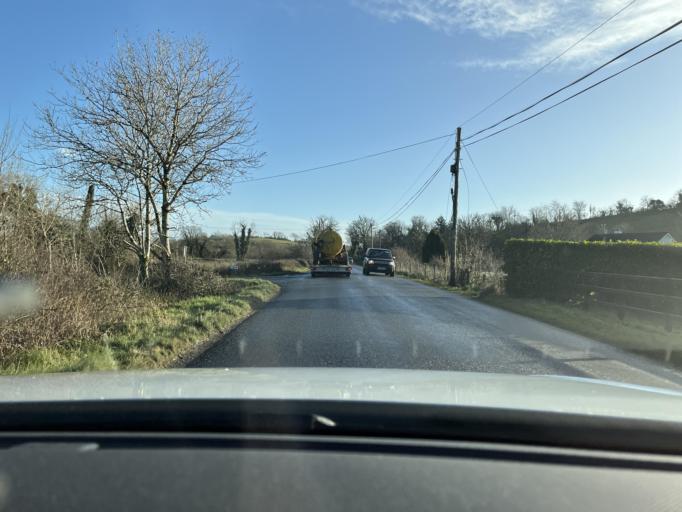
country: IE
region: Connaught
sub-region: County Leitrim
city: Manorhamilton
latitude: 54.1939
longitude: -8.1713
